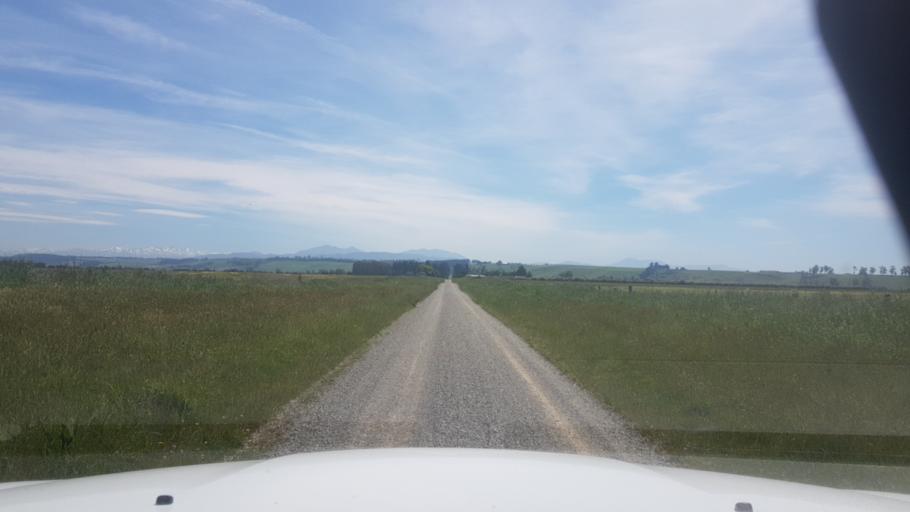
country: NZ
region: Canterbury
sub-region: Timaru District
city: Pleasant Point
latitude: -44.2310
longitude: 171.1666
